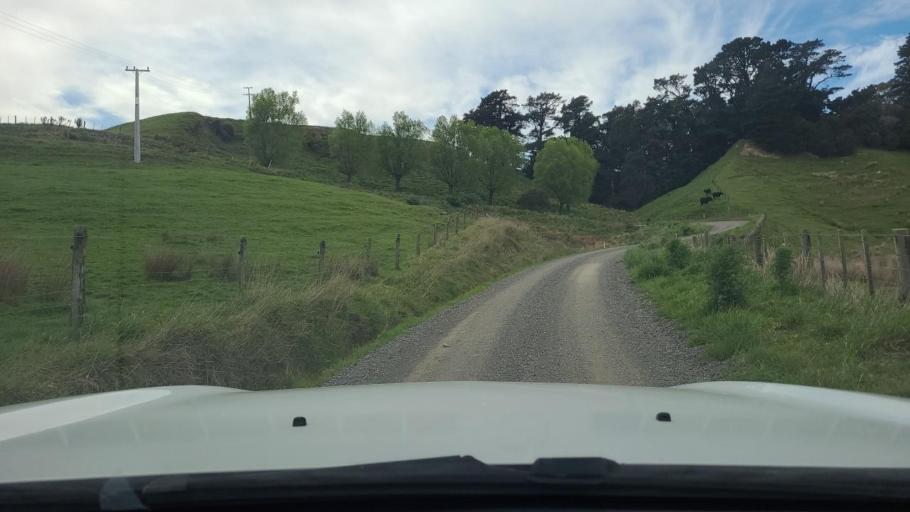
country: NZ
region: Wellington
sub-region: South Wairarapa District
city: Waipawa
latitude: -41.3865
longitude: 175.5191
